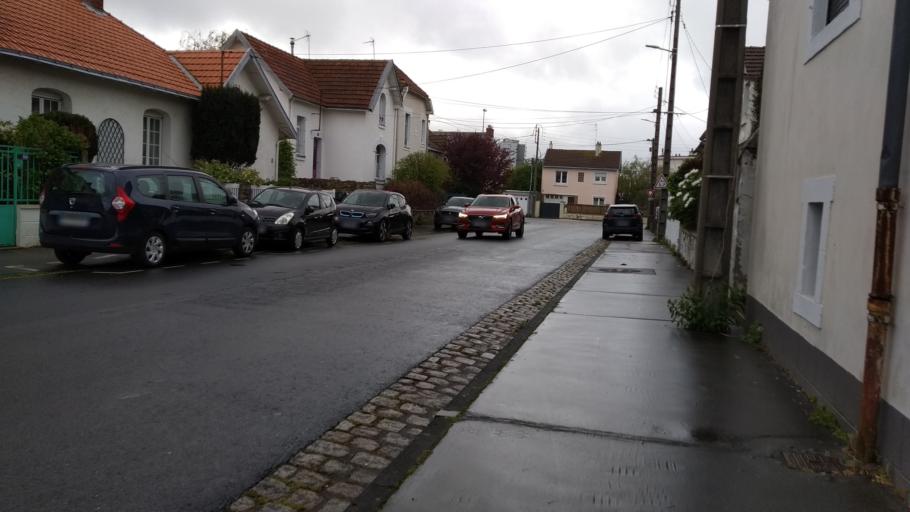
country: FR
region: Pays de la Loire
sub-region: Departement de la Loire-Atlantique
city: Nantes
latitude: 47.2144
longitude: -1.5915
